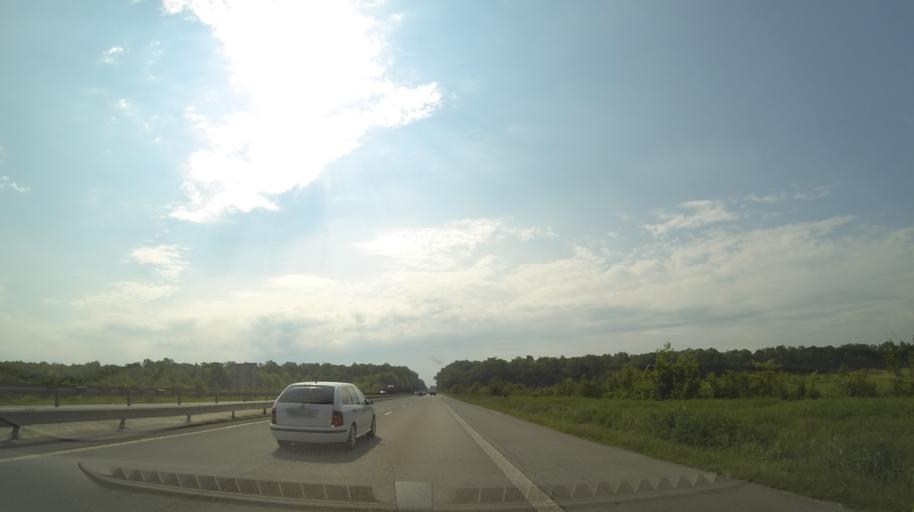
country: RO
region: Giurgiu
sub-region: Comuna Vanatorii Mici
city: Vanatorii Mici
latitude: 44.5140
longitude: 25.5619
